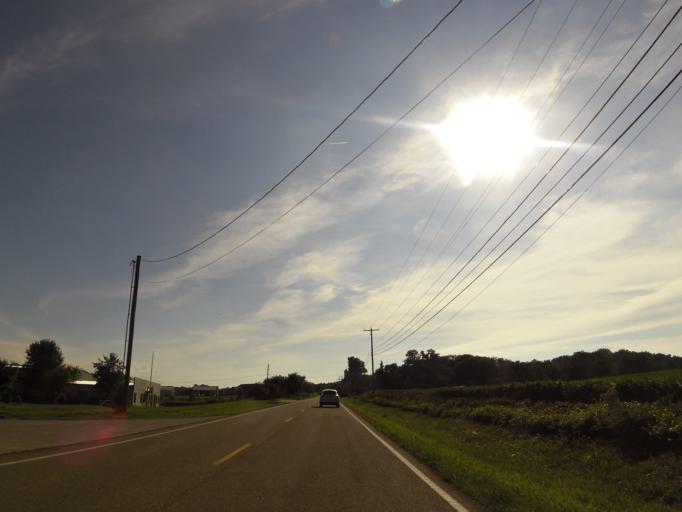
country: US
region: Tennessee
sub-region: Blount County
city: Louisville
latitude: 35.8174
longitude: -84.0641
